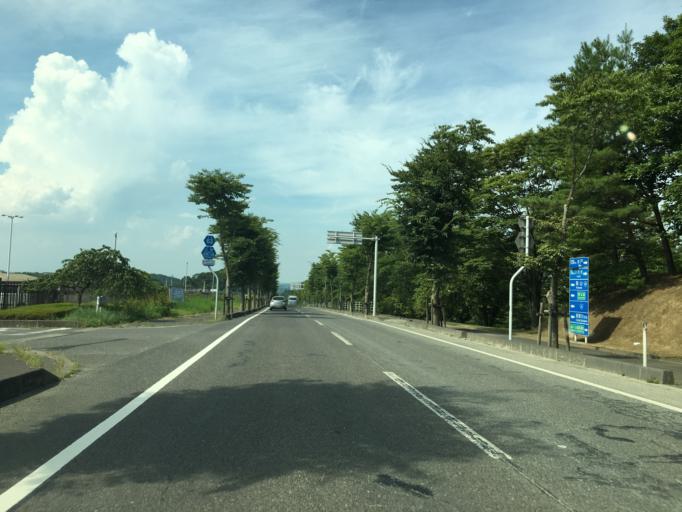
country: JP
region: Fukushima
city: Sukagawa
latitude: 37.2286
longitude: 140.4352
